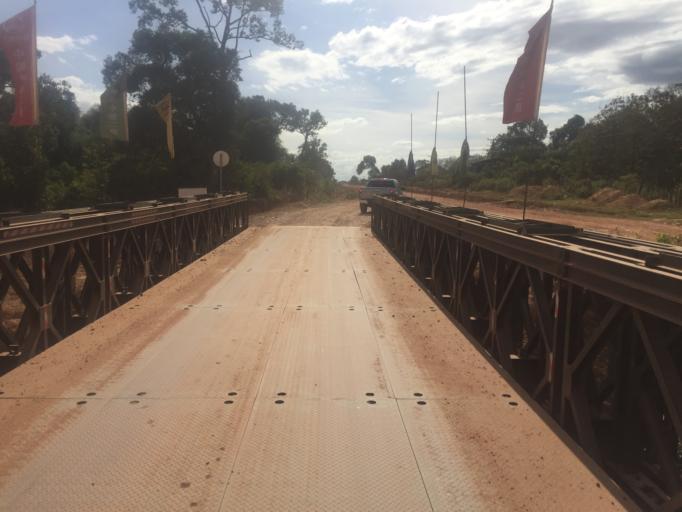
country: LA
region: Attapu
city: Attapu
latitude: 14.7960
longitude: 106.7531
